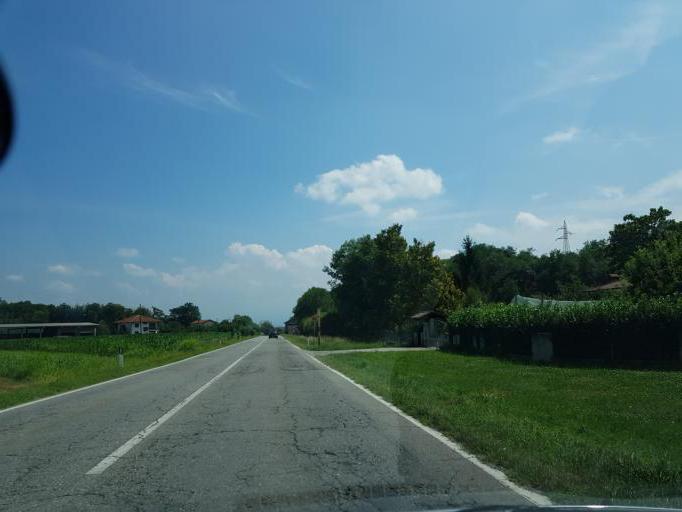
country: IT
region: Piedmont
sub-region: Provincia di Cuneo
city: Montemale di Cuneo
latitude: 44.4441
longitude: 7.4051
